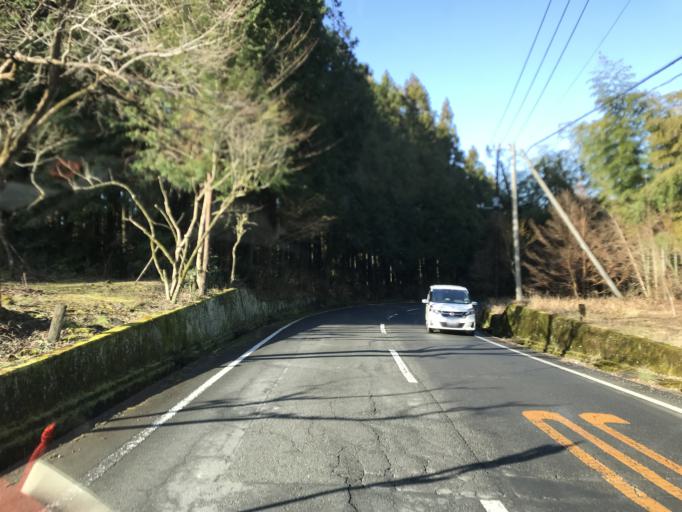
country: JP
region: Shizuoka
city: Fuji
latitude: 35.2481
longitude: 138.6962
